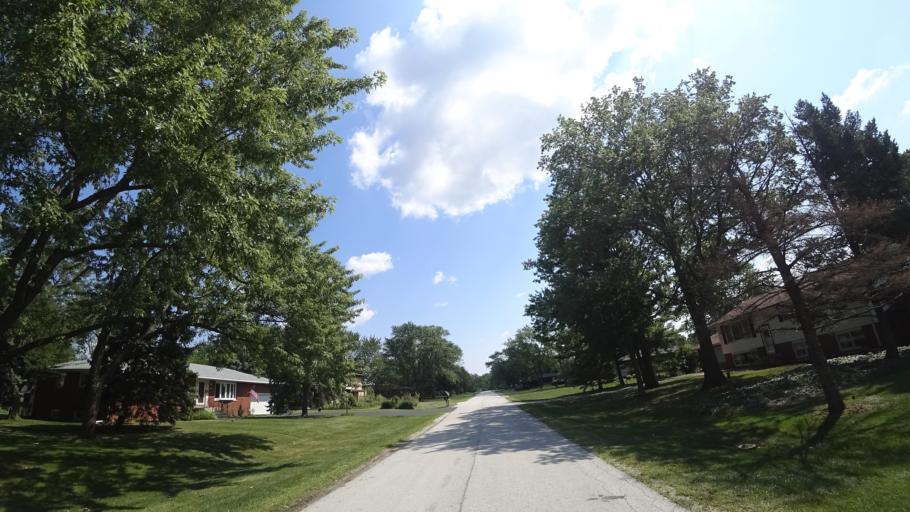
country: US
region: Illinois
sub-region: Cook County
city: Tinley Park
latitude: 41.6046
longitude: -87.7891
